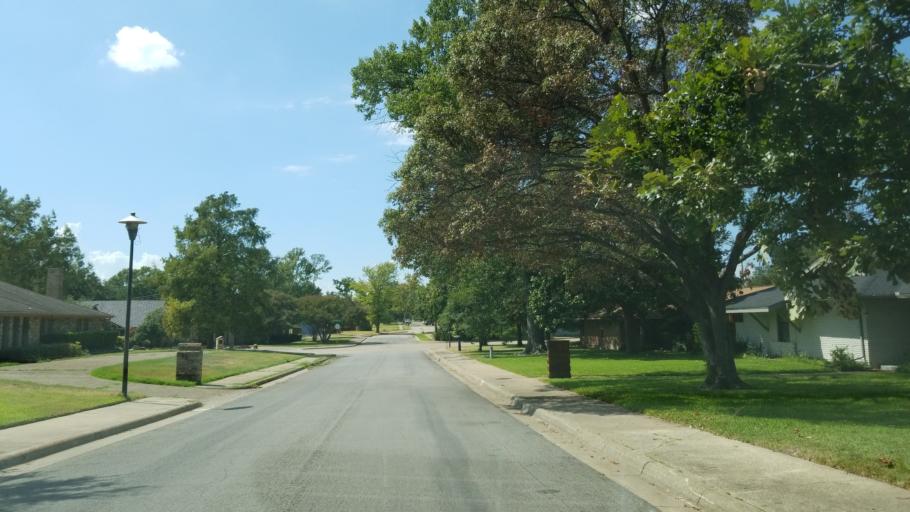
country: US
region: Texas
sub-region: Dallas County
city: Addison
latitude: 32.9541
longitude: -96.7907
